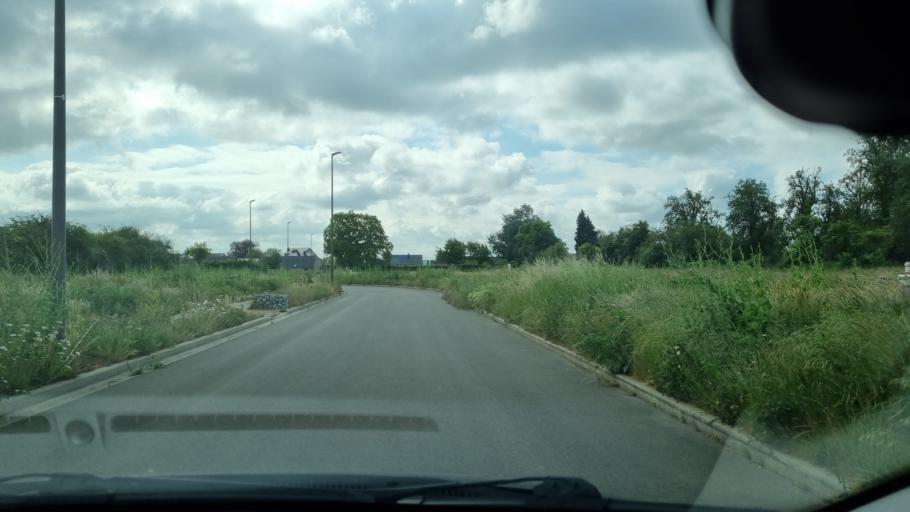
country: BE
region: Wallonia
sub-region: Province de Liege
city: Bassenge
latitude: 50.7378
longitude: 5.6022
